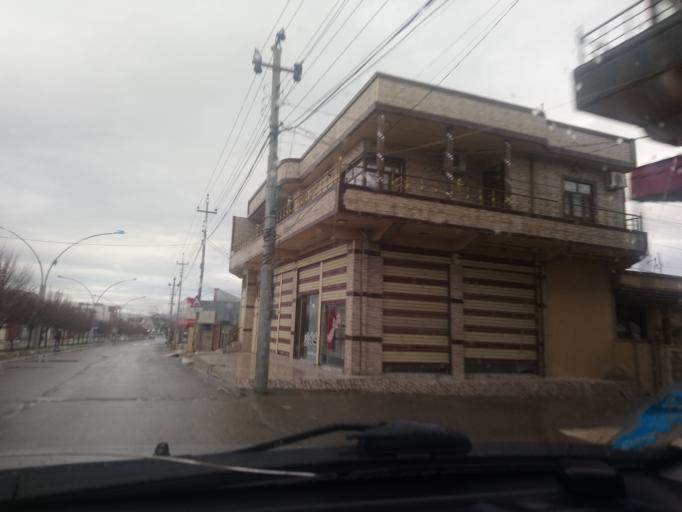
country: IQ
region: As Sulaymaniyah
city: Qeladize
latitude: 36.1776
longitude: 45.1420
